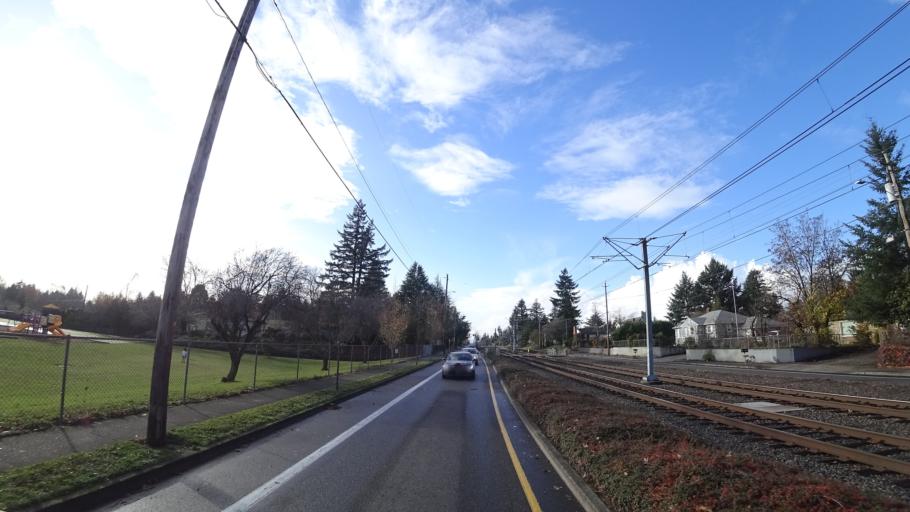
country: US
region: Oregon
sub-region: Multnomah County
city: Lents
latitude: 45.5225
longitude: -122.5440
